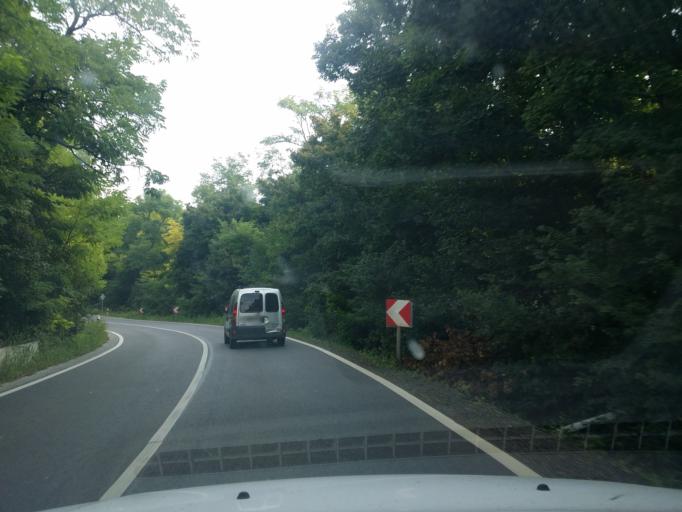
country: HU
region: Pest
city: Acsa
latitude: 47.7861
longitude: 19.3657
